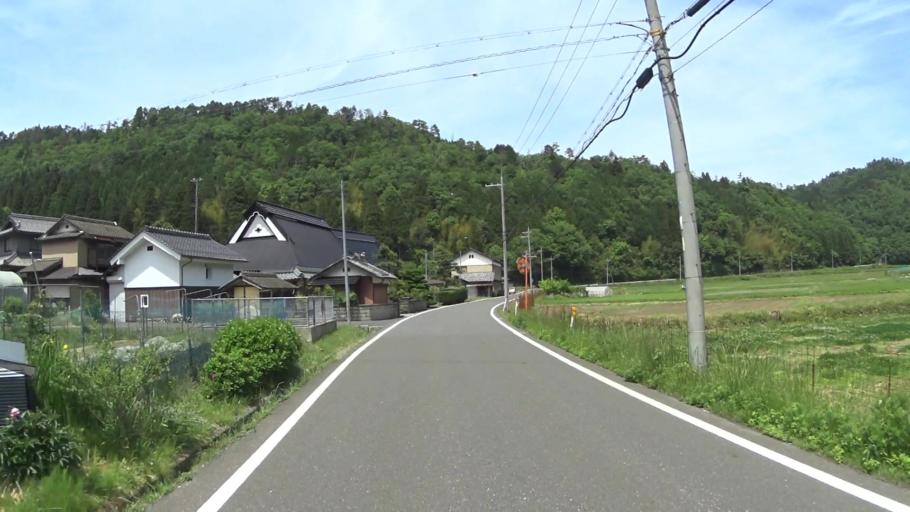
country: JP
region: Kyoto
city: Maizuru
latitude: 35.3880
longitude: 135.4620
